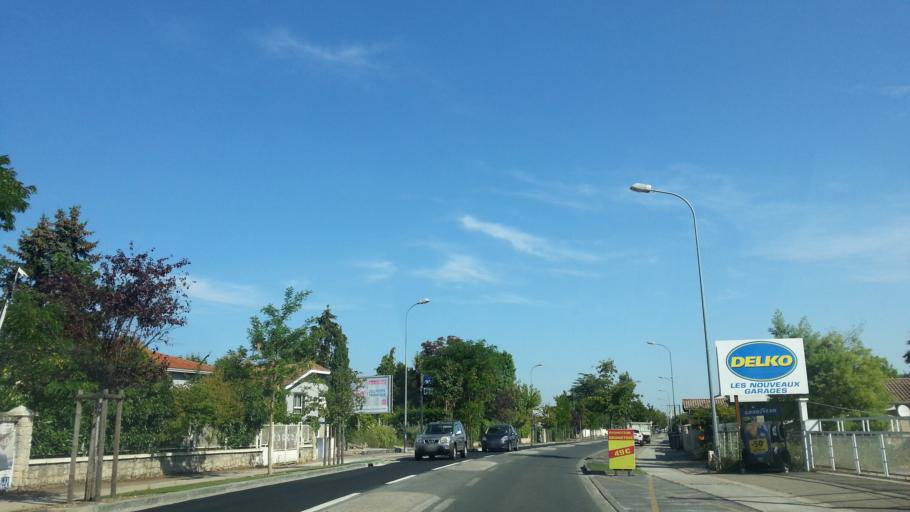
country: FR
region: Aquitaine
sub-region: Departement de la Gironde
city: Villenave-d'Ornon
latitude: 44.7669
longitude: -0.5633
